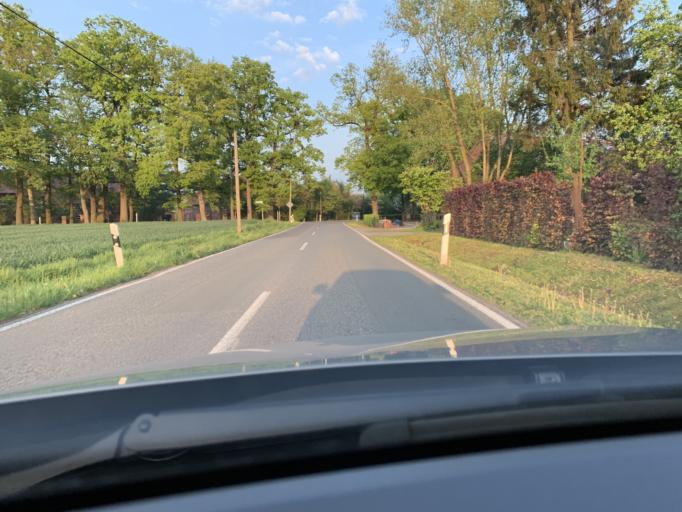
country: DE
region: North Rhine-Westphalia
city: Rietberg
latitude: 51.8015
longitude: 8.3866
